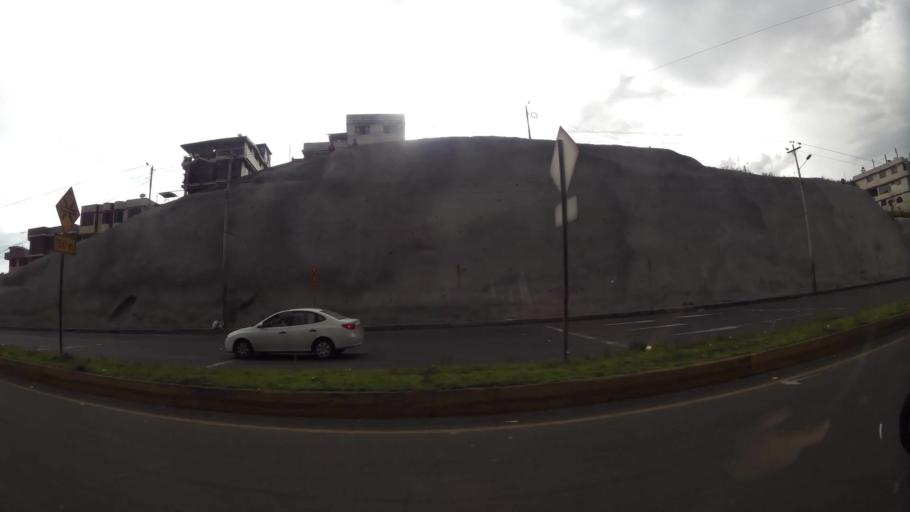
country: EC
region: Pichincha
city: Machachi
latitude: -0.4036
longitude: -78.5459
